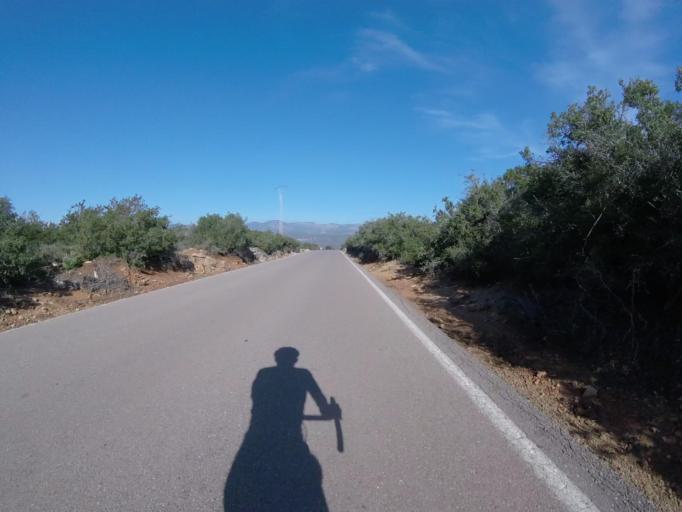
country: ES
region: Valencia
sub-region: Provincia de Castello
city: Benlloch
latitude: 40.2380
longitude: 0.0725
